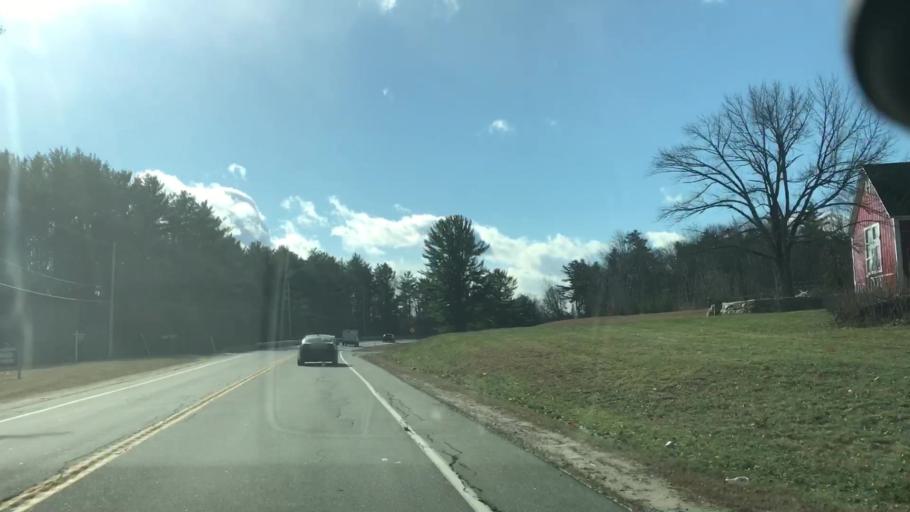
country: US
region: New Hampshire
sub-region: Carroll County
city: Wolfeboro
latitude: 43.6131
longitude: -71.1766
